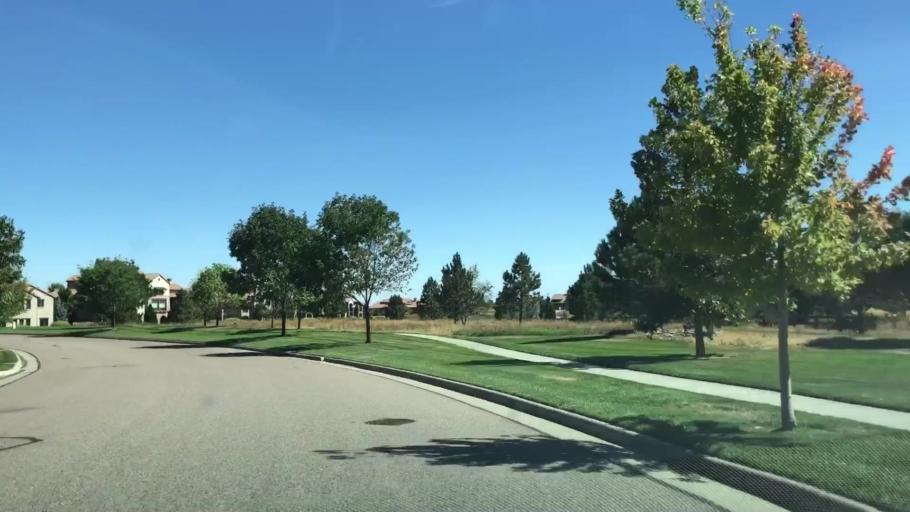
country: US
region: Colorado
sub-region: Weld County
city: Windsor
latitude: 40.5307
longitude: -104.9561
